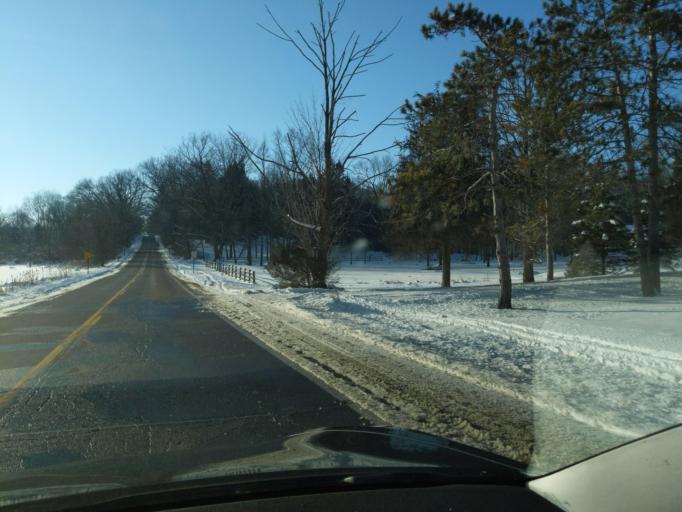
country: US
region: Michigan
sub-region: Ingham County
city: Stockbridge
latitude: 42.4680
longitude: -84.1081
